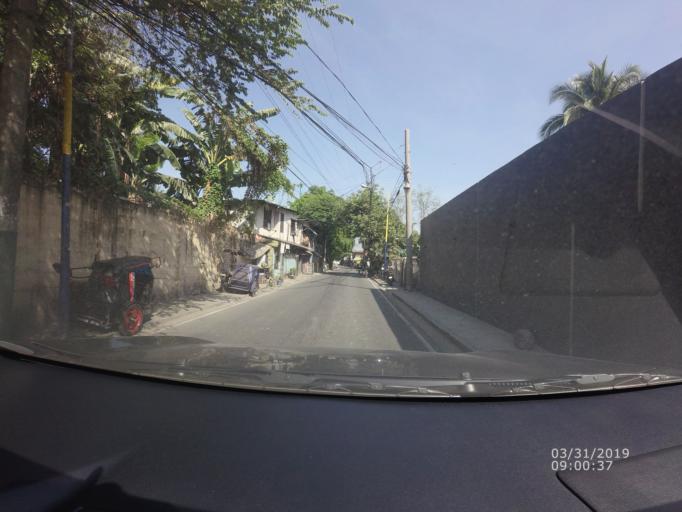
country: PH
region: Metro Manila
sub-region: Mandaluyong
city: Mandaluyong City
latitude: 14.5755
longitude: 121.0253
